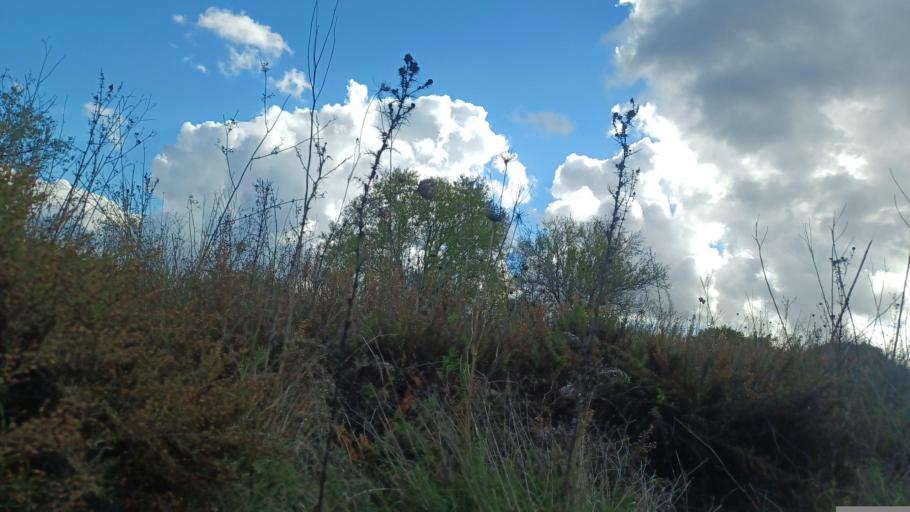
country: CY
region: Pafos
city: Mesogi
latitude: 34.8487
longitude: 32.5169
